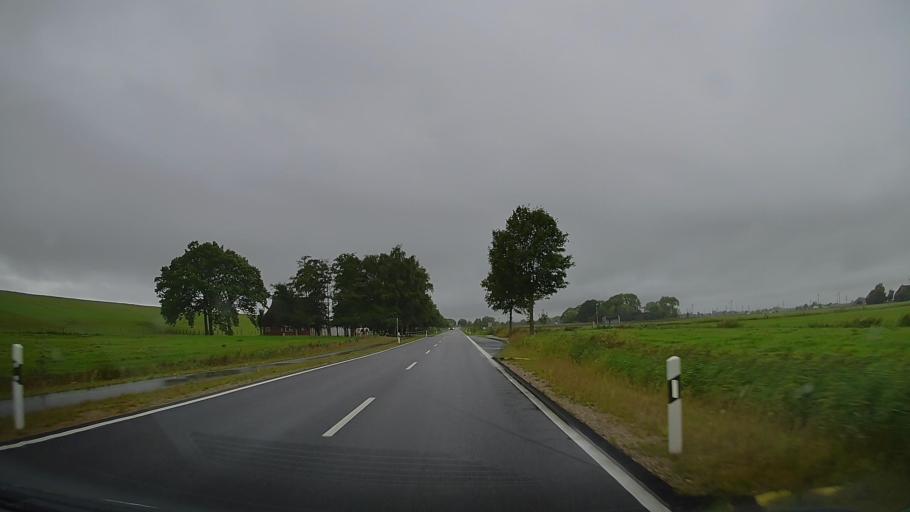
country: DE
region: Schleswig-Holstein
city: Sankt Margarethen
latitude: 53.8757
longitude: 9.2868
